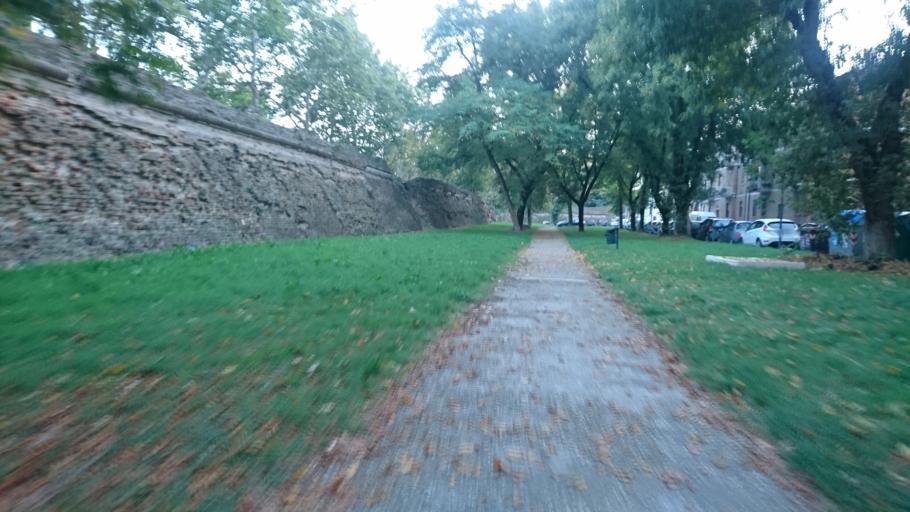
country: IT
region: Emilia-Romagna
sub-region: Provincia di Ferrara
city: Ferrara
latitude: 44.8454
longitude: 11.6105
